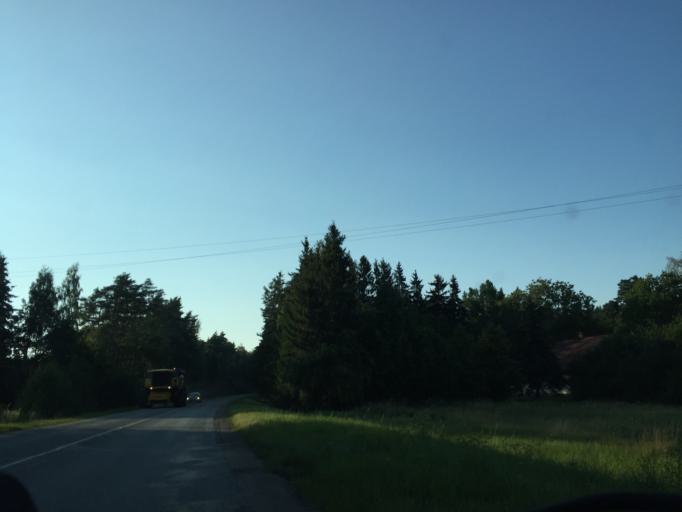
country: LV
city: Tervete
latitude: 56.4566
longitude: 23.4084
